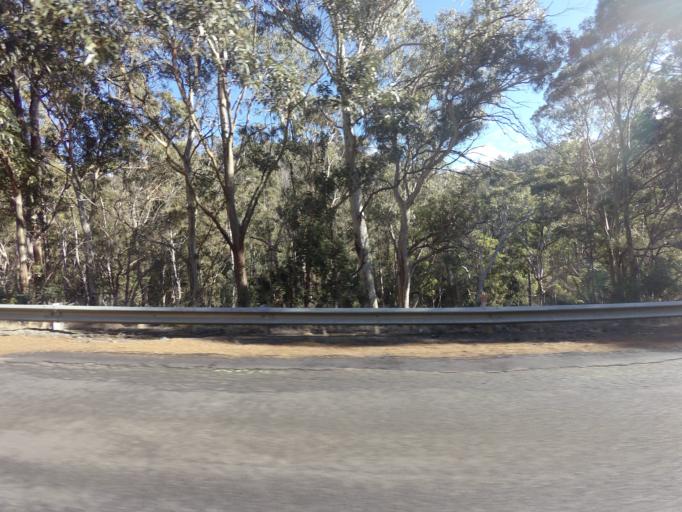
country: AU
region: Tasmania
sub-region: Glenorchy
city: Berriedale
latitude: -42.8243
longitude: 147.2100
